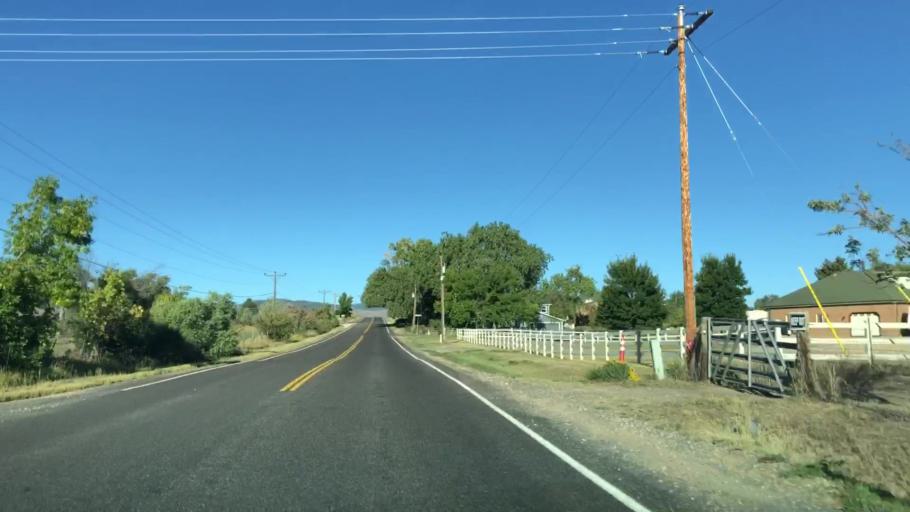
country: US
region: Colorado
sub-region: Larimer County
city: Loveland
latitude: 40.3785
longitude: -105.1538
